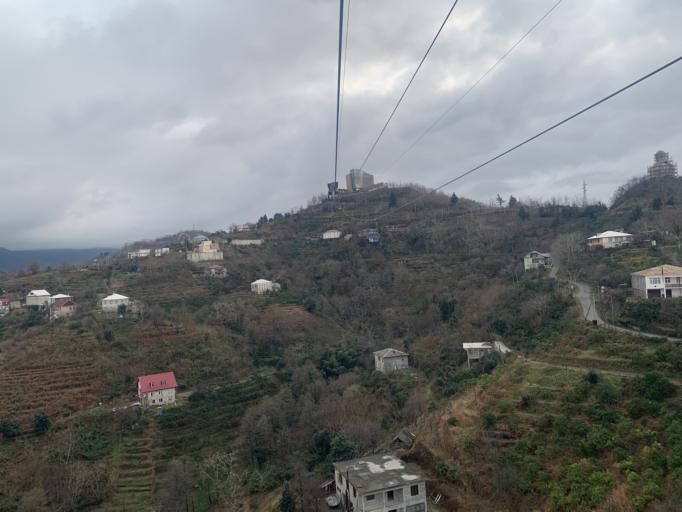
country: GE
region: Ajaria
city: Batumi
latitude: 41.6308
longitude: 41.6536
